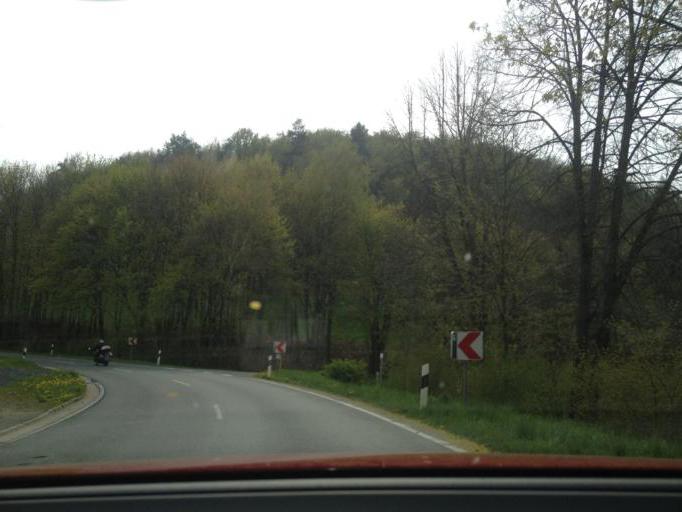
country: DE
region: Bavaria
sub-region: Upper Franconia
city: Goldkronach
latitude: 50.0256
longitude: 11.6914
